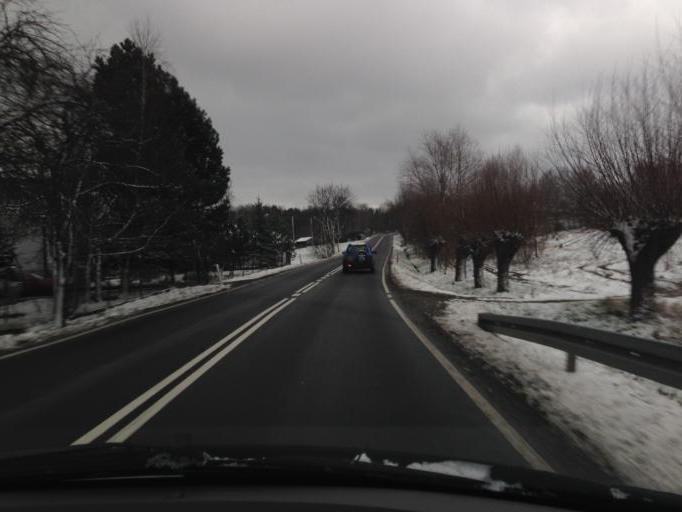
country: PL
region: Lesser Poland Voivodeship
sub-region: Powiat tarnowski
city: Siemiechow
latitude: 49.8489
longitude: 20.9298
